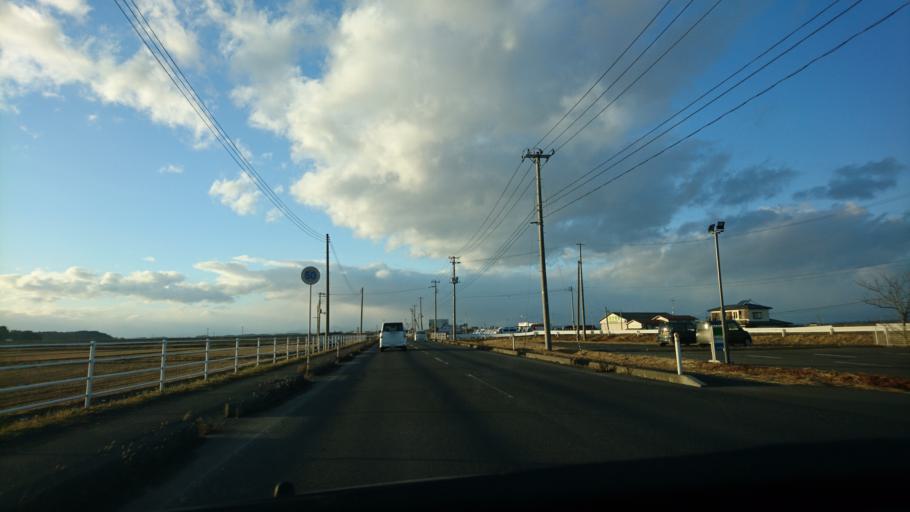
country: JP
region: Miyagi
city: Wakuya
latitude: 38.7163
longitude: 141.1650
